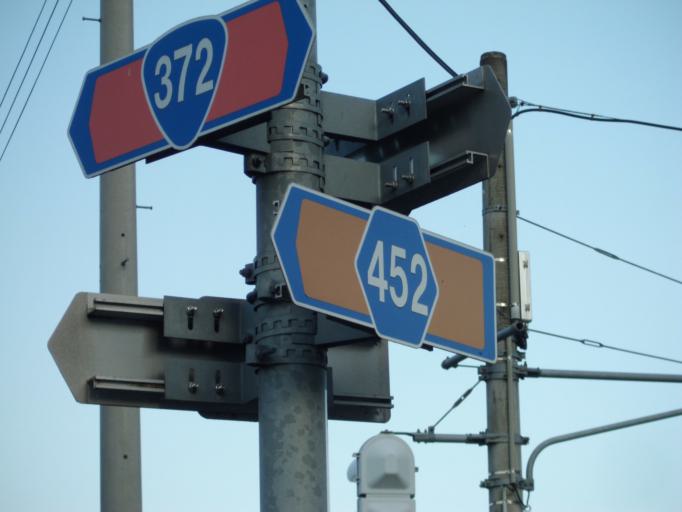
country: JP
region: Kyoto
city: Kameoka
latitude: 35.0628
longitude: 135.4530
